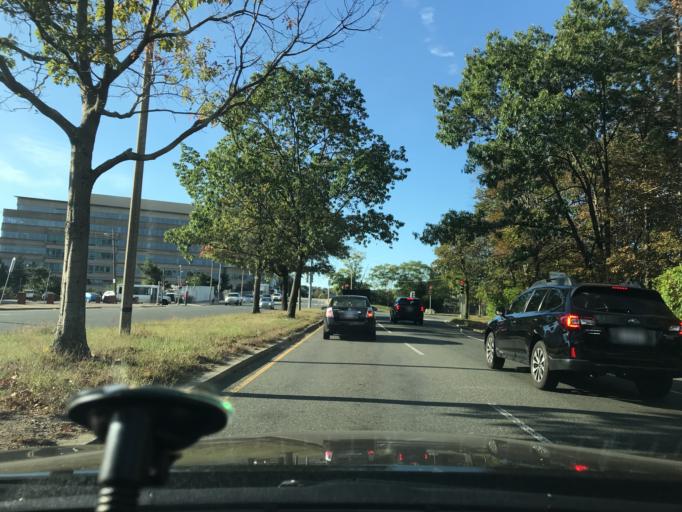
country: US
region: Massachusetts
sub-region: Middlesex County
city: Watertown
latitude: 42.3596
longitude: -71.1472
